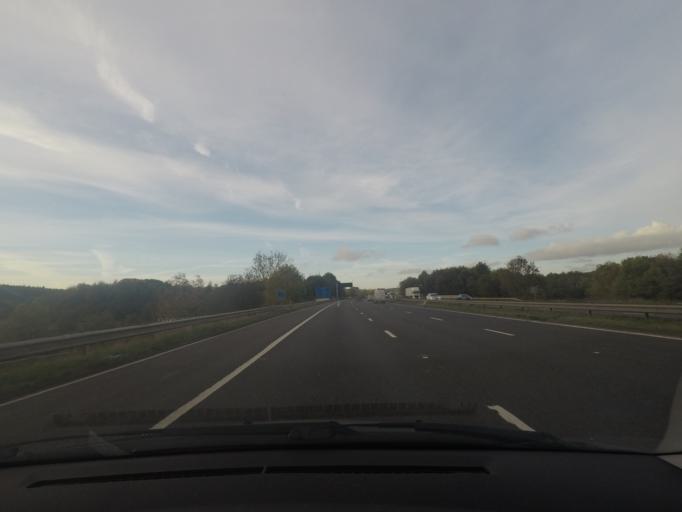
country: GB
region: England
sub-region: Barnsley
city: Darton
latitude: 53.6014
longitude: -1.5502
